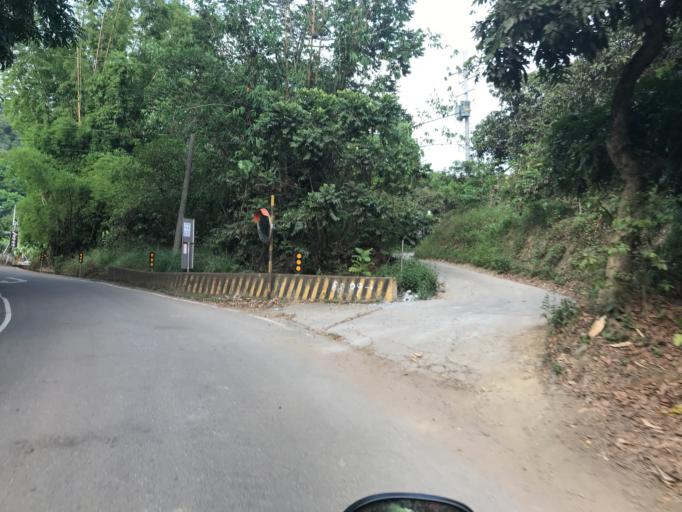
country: TW
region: Taiwan
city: Zhongxing New Village
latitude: 24.0409
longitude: 120.7054
